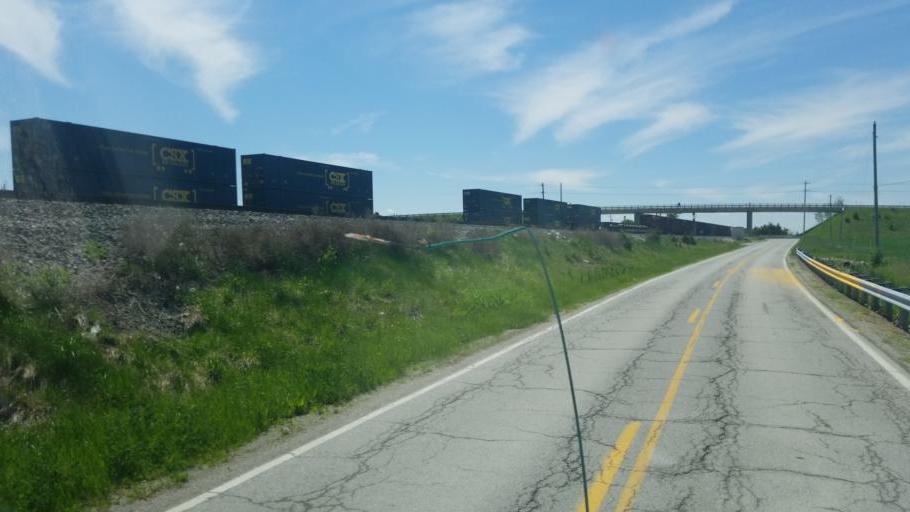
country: US
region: Ohio
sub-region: Huron County
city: Willard
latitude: 41.0699
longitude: -82.7805
